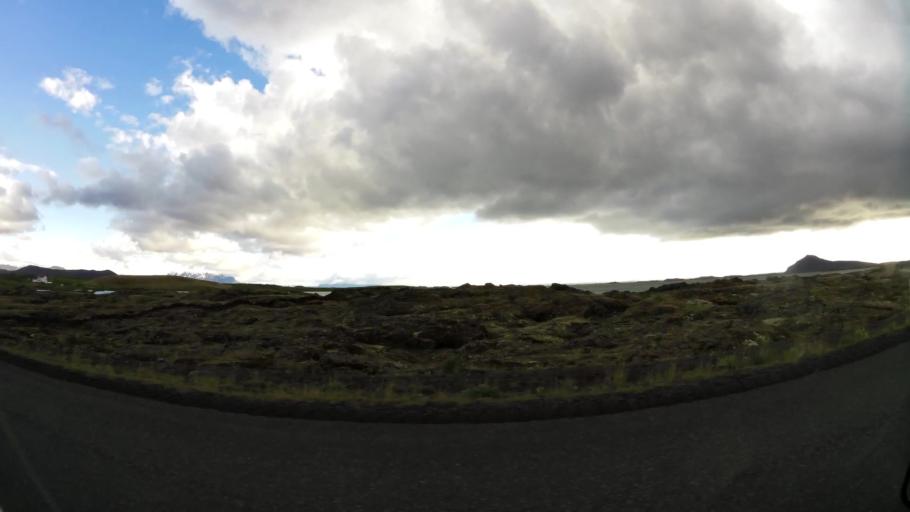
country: IS
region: Northeast
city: Laugar
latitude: 65.6452
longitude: -16.9190
